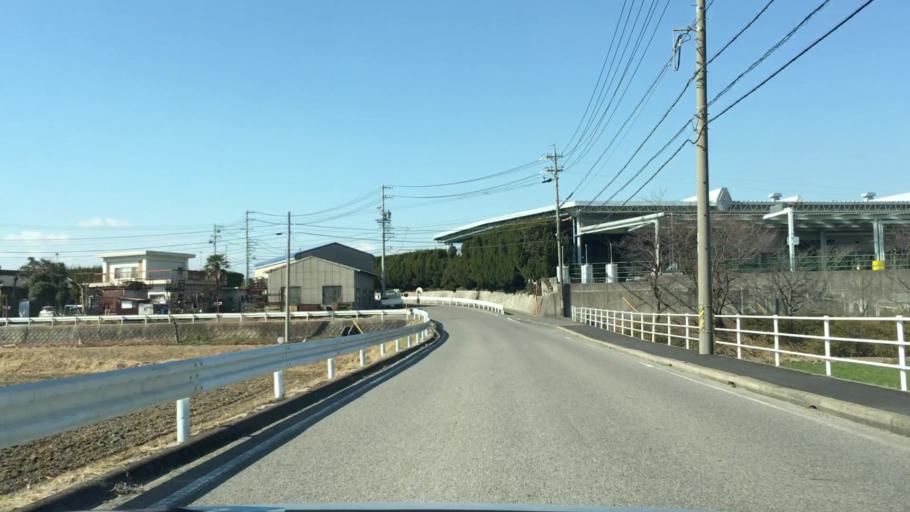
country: JP
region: Aichi
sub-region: Toyota-shi
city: Toyota
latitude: 35.0332
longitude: 137.1275
